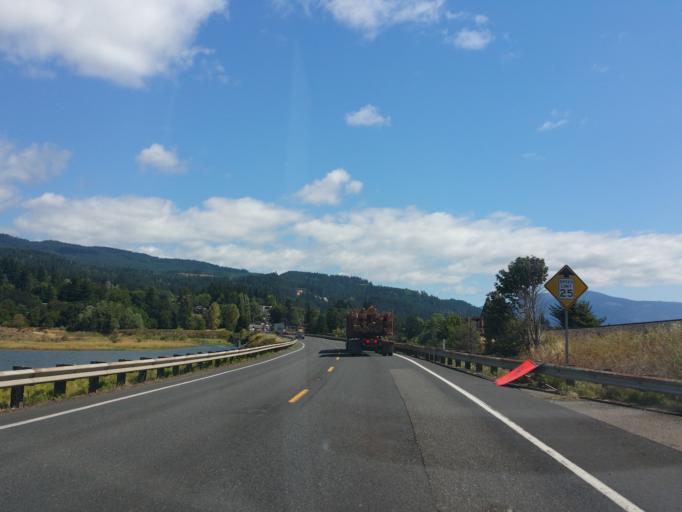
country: US
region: Washington
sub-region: Skamania County
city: Stevenson
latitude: 45.6878
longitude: -121.8915
